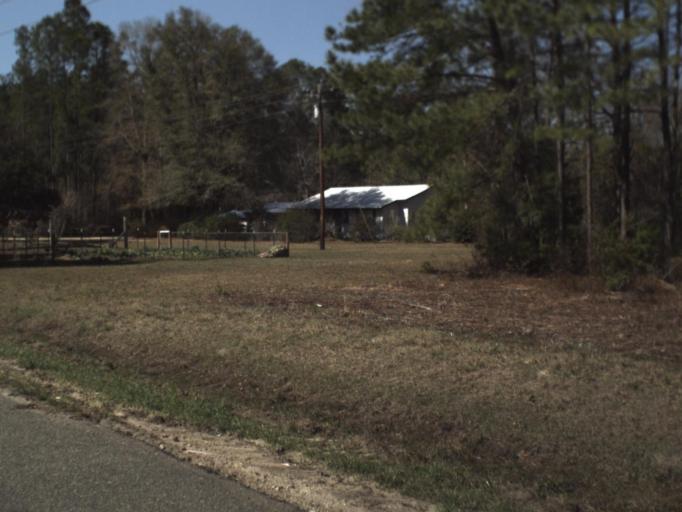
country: US
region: Florida
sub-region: Calhoun County
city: Blountstown
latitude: 30.4699
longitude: -85.0860
